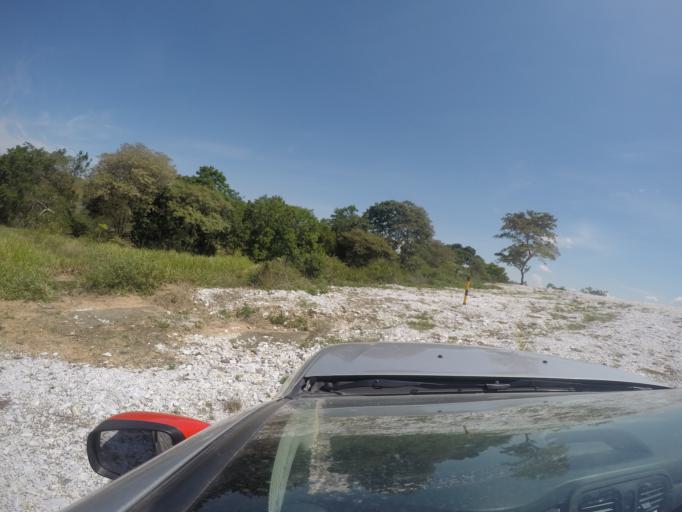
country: CO
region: Antioquia
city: Puerto Triunfo
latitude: 5.9139
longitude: -74.7205
